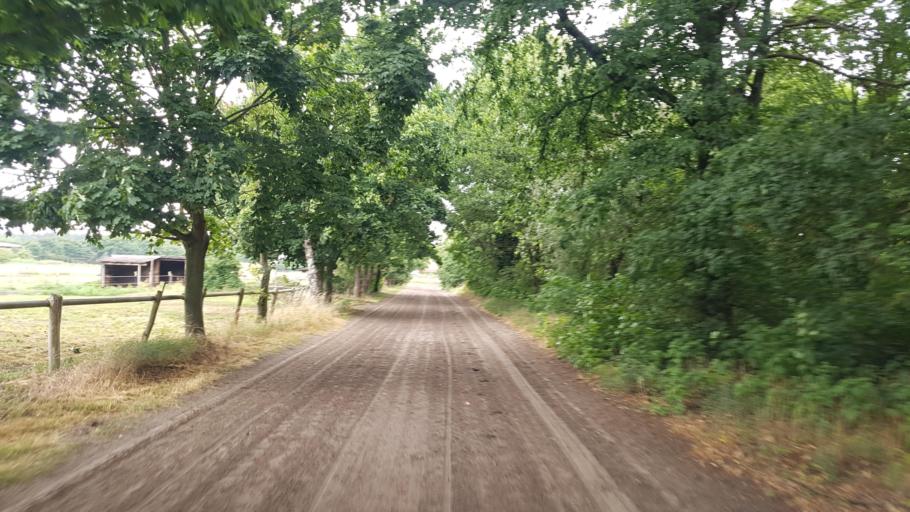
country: DE
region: Brandenburg
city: Trebbin
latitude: 52.2521
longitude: 13.1615
